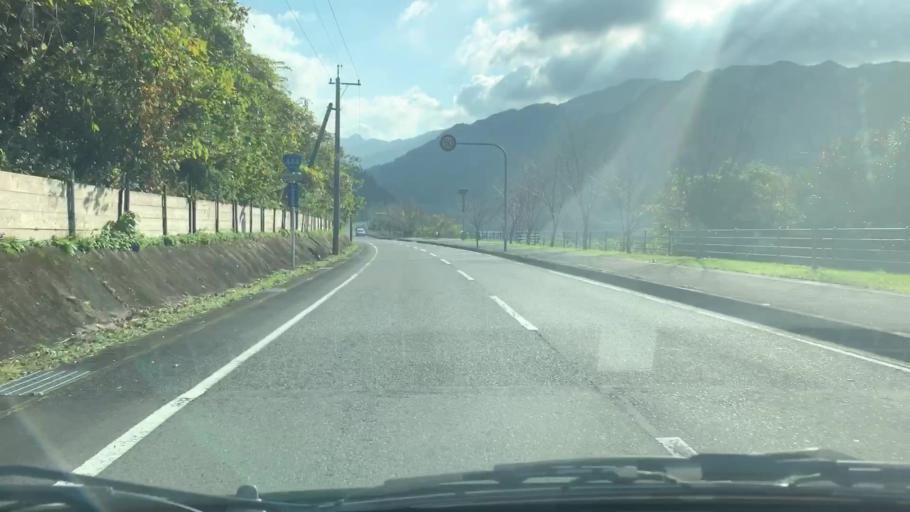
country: JP
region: Saga Prefecture
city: Kashima
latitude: 33.0369
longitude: 130.0706
